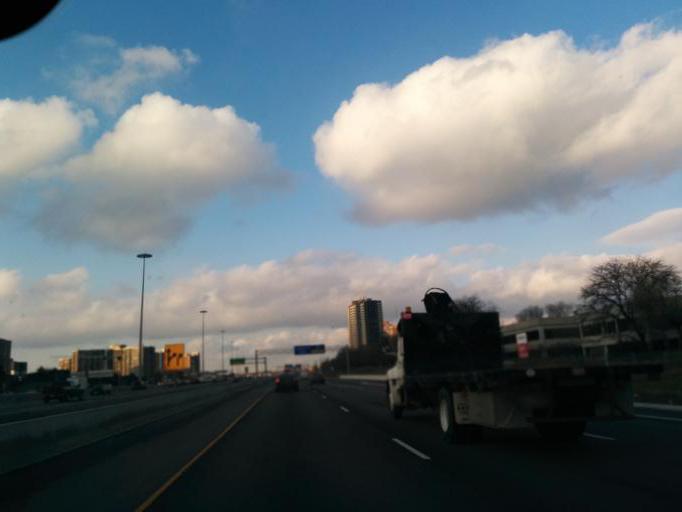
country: CA
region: Ontario
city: Etobicoke
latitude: 43.6461
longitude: -79.5632
